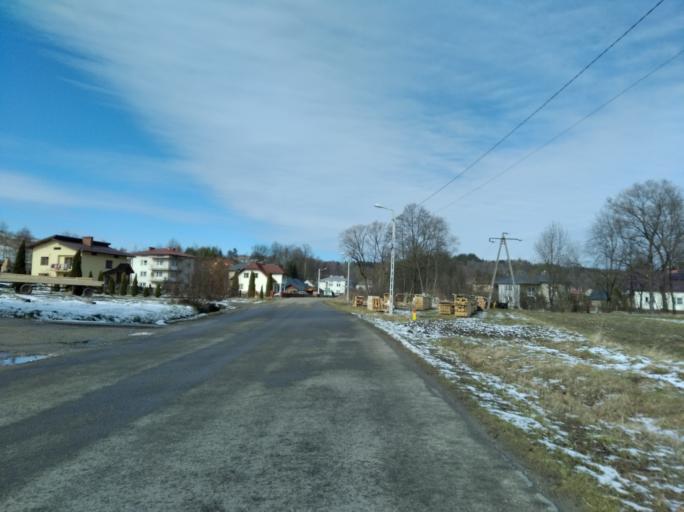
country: PL
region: Subcarpathian Voivodeship
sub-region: Powiat brzozowski
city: Jasienica Rosielna
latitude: 49.7528
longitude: 21.9132
